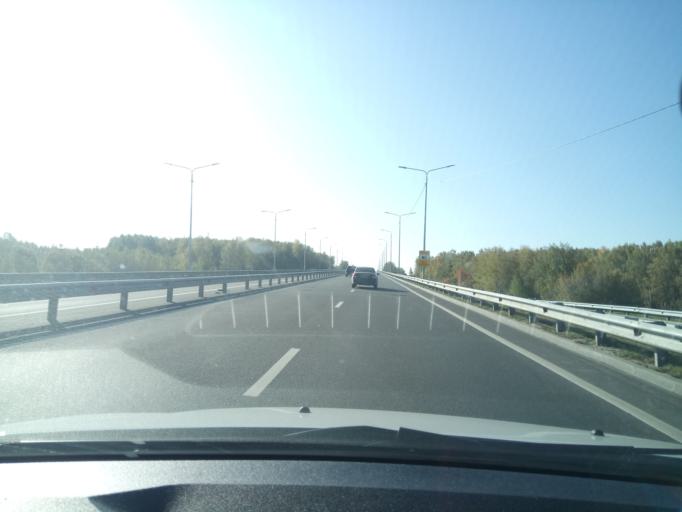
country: RU
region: Nizjnij Novgorod
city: Burevestnik
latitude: 56.0064
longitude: 43.9665
